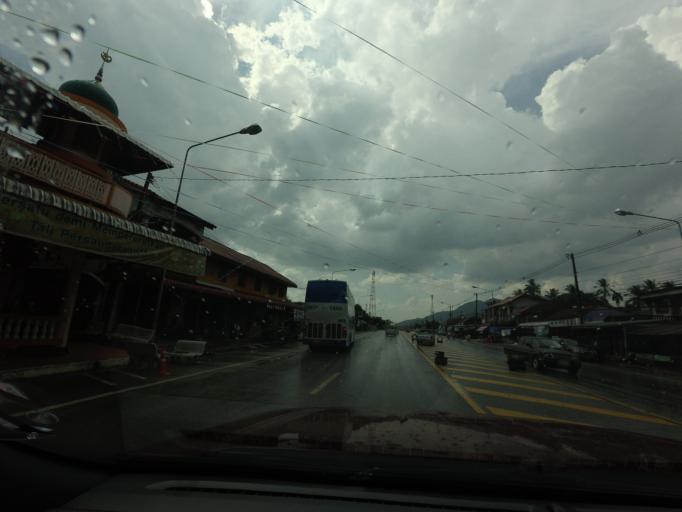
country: TH
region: Yala
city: Krong Pi Nang
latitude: 6.4180
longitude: 101.2791
